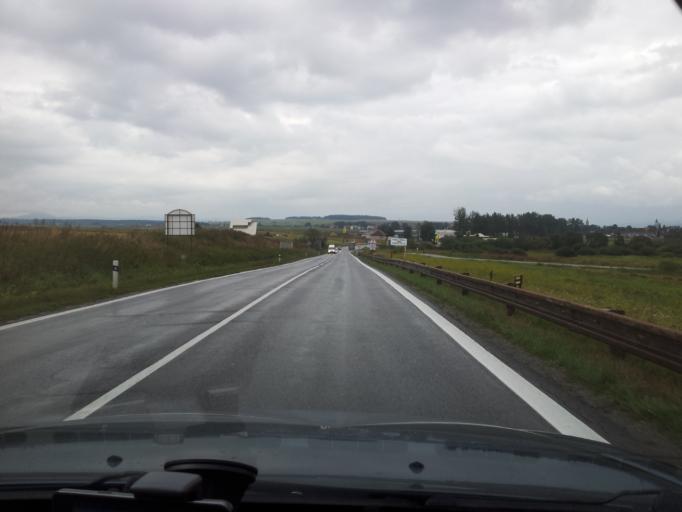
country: SK
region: Presovsky
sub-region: Okres Poprad
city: Poprad
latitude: 49.1016
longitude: 20.3432
